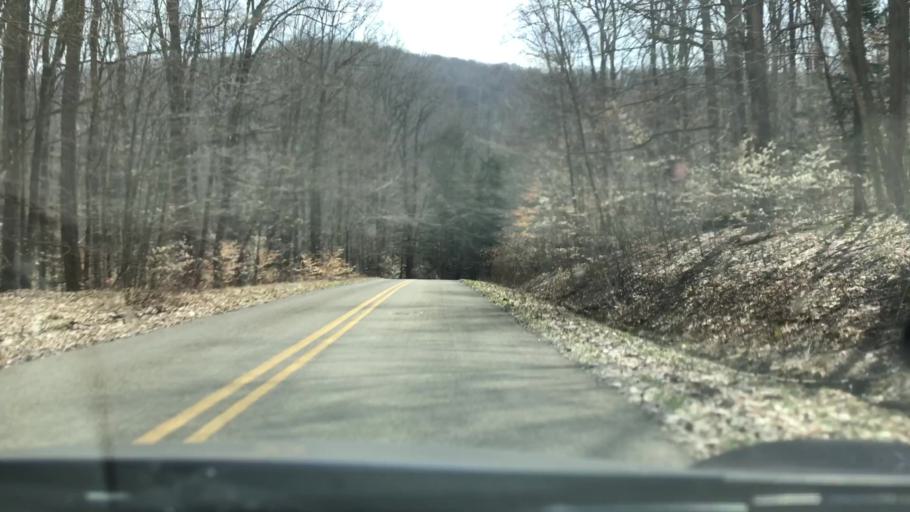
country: US
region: Pennsylvania
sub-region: Warren County
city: Sheffield
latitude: 41.8128
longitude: -78.9379
